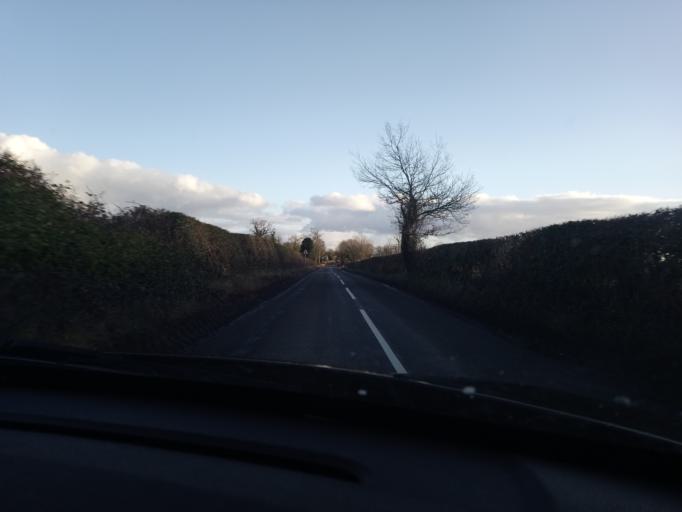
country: GB
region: England
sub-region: Shropshire
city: Petton
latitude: 52.8775
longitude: -2.7841
